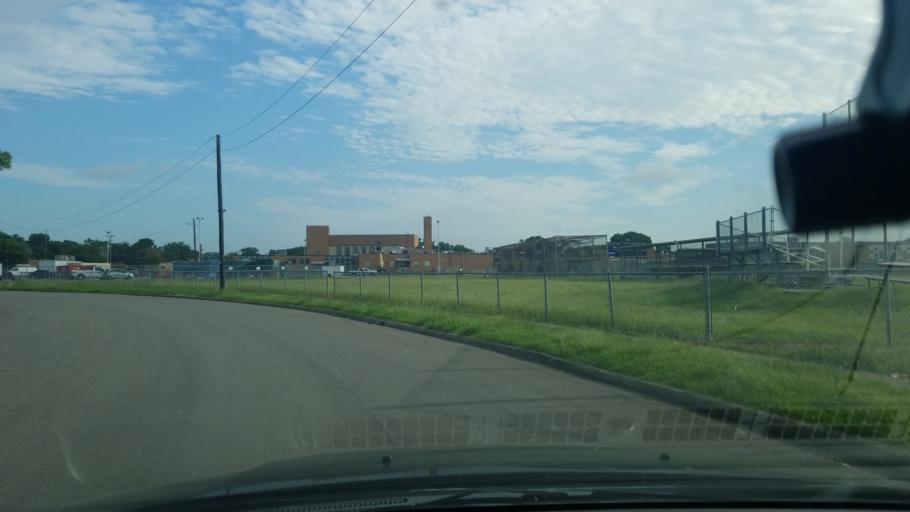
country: US
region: Texas
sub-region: Dallas County
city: Balch Springs
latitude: 32.7438
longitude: -96.6691
